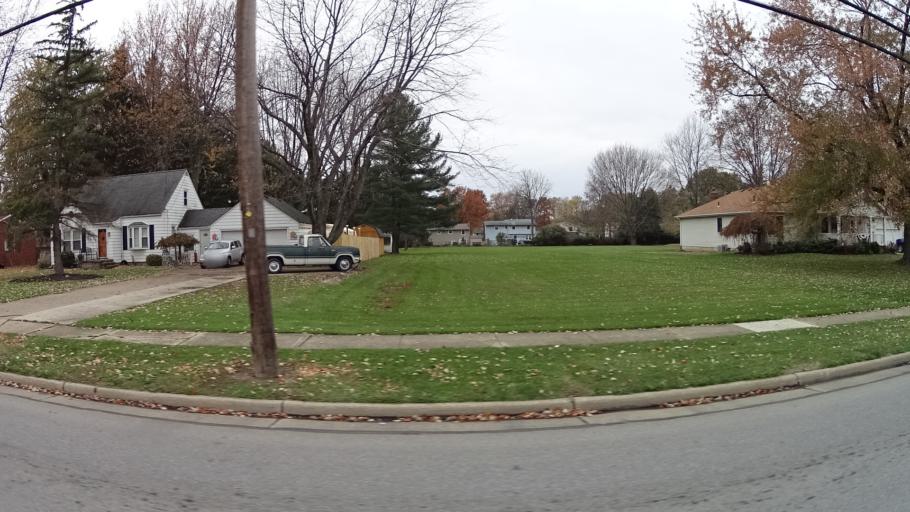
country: US
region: Ohio
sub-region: Lorain County
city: Sheffield
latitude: 41.3988
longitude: -82.0773
